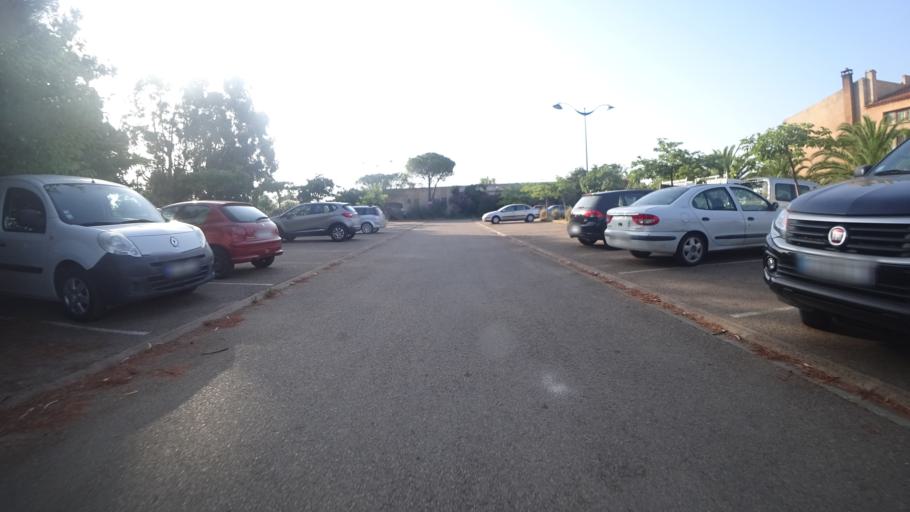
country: FR
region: Corsica
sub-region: Departement de la Corse-du-Sud
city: Porto-Vecchio
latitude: 41.6387
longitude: 9.3470
